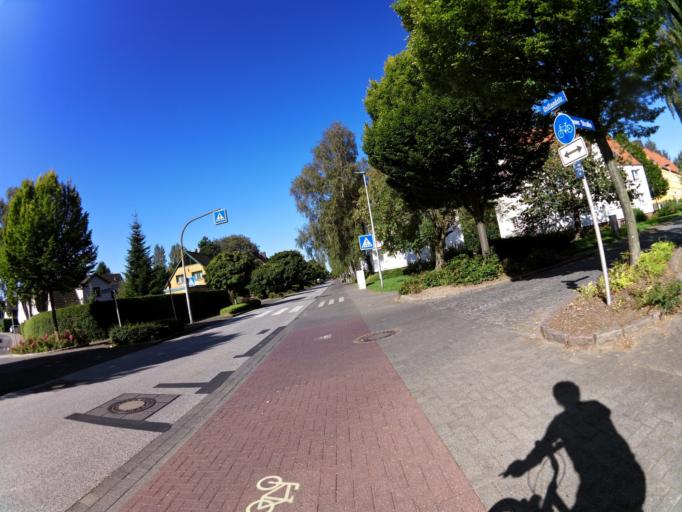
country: DE
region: Schleswig-Holstein
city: Barkelsby
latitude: 54.4838
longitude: 9.8303
